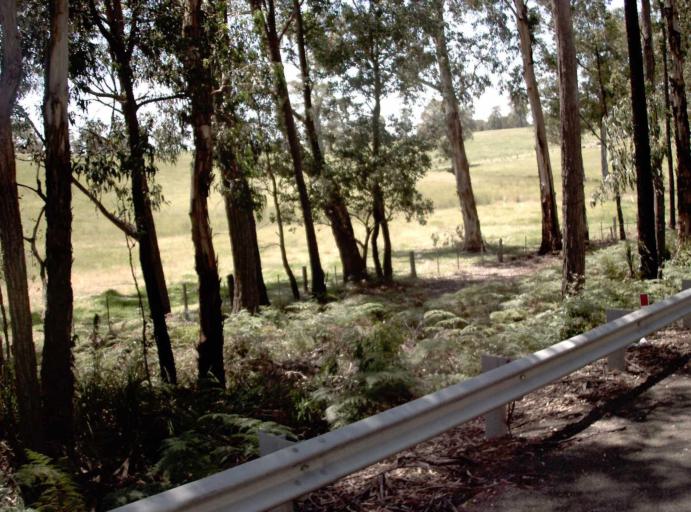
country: AU
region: Victoria
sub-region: East Gippsland
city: Lakes Entrance
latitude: -37.7297
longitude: 148.1308
